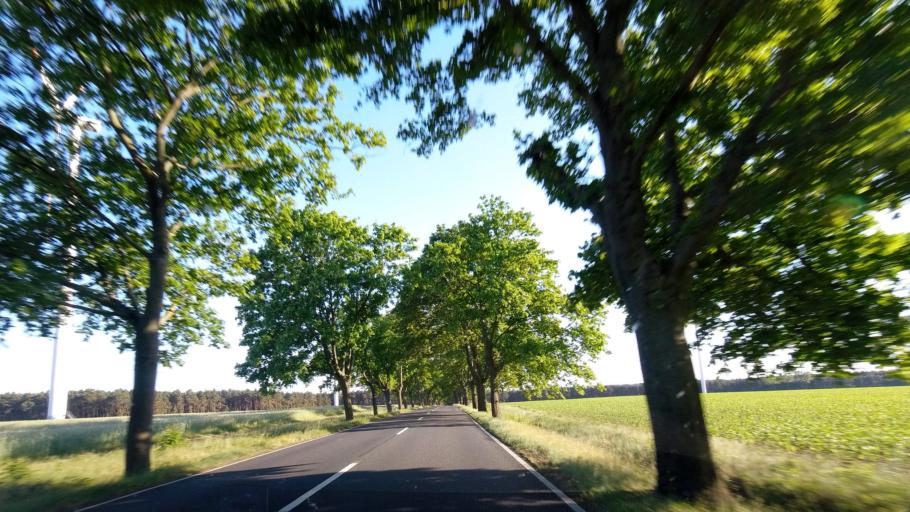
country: DE
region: Brandenburg
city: Golzow
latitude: 52.3093
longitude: 12.6085
